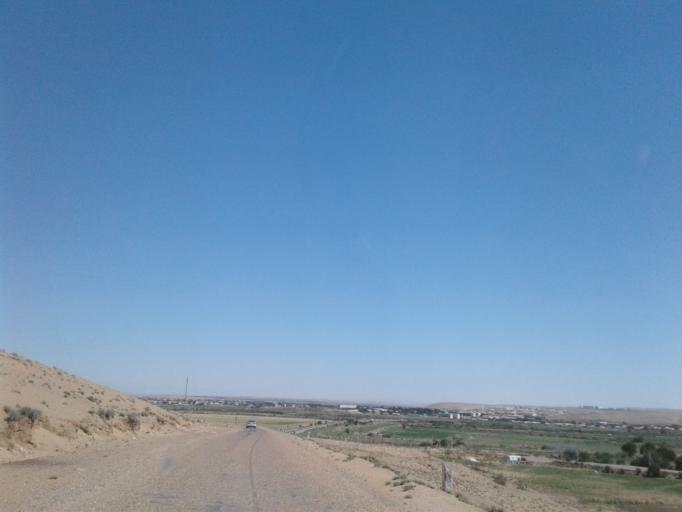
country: AF
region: Badghis
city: Bala Murghab
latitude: 35.9766
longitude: 62.9002
